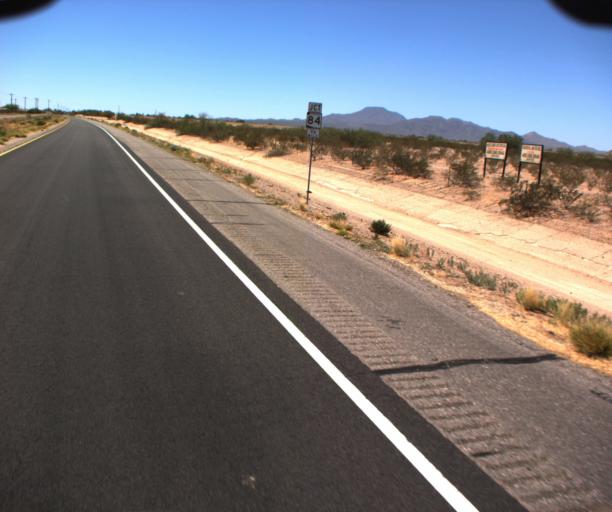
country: US
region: Arizona
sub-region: Pinal County
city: Maricopa
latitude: 32.8856
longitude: -112.0496
